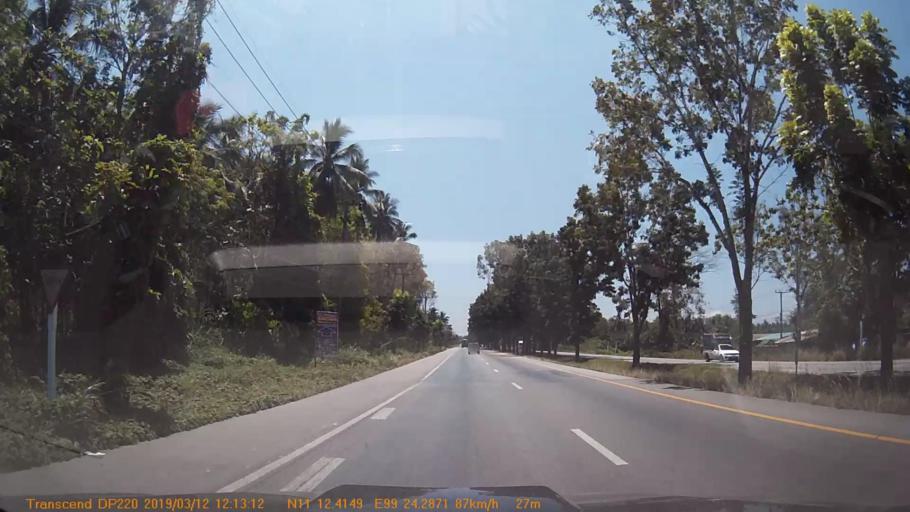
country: TH
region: Prachuap Khiri Khan
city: Bang Saphan
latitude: 11.2069
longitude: 99.4048
